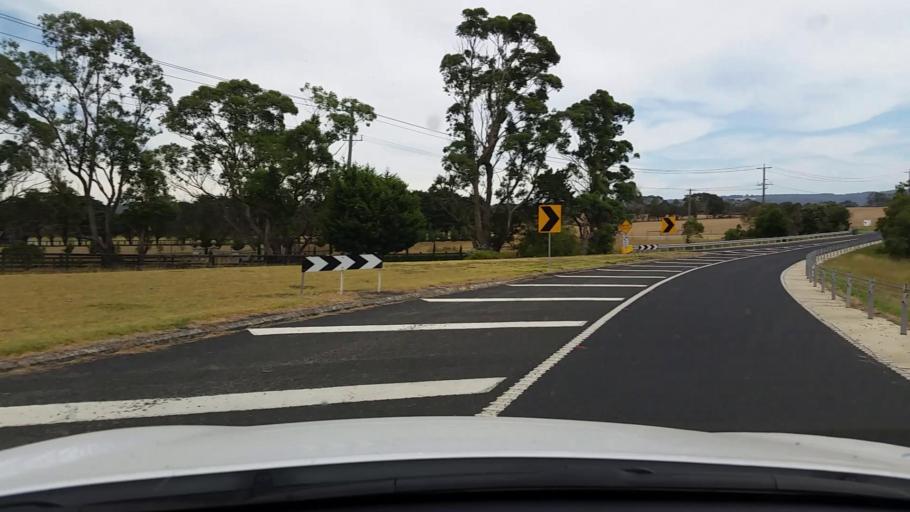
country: AU
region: Victoria
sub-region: Mornington Peninsula
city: Safety Beach
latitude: -38.3098
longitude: 145.0295
